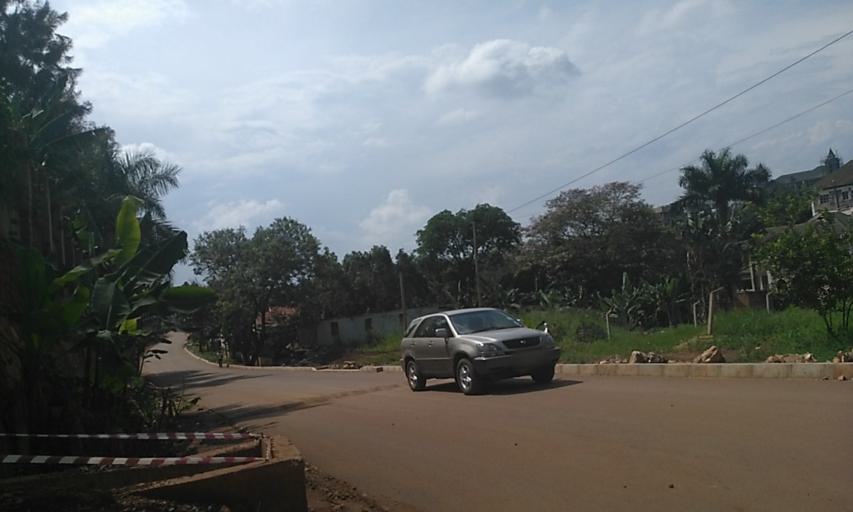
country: UG
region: Central Region
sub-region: Wakiso District
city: Kireka
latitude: 0.3516
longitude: 32.6129
